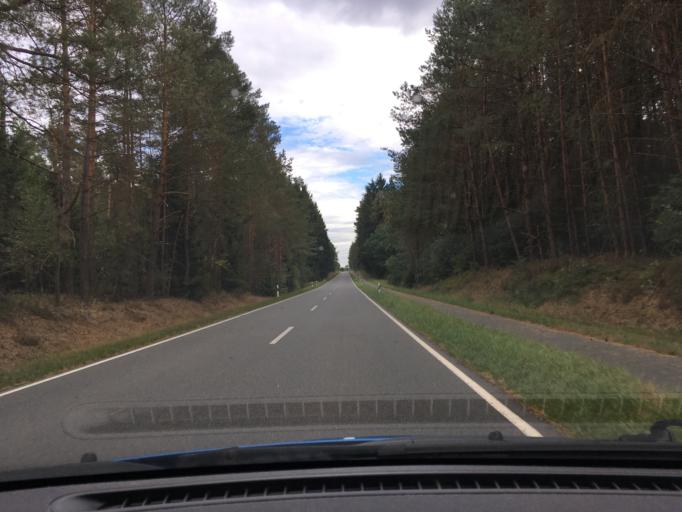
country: DE
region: Lower Saxony
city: Jesteburg
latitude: 53.2531
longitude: 9.9153
